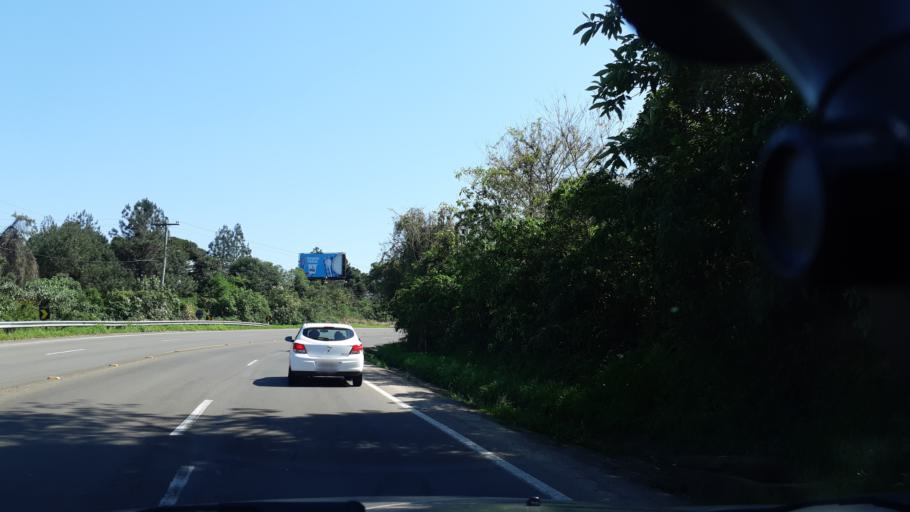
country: BR
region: Rio Grande do Sul
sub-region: Nova Petropolis
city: Nova Petropolis
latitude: -29.3917
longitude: -51.1257
